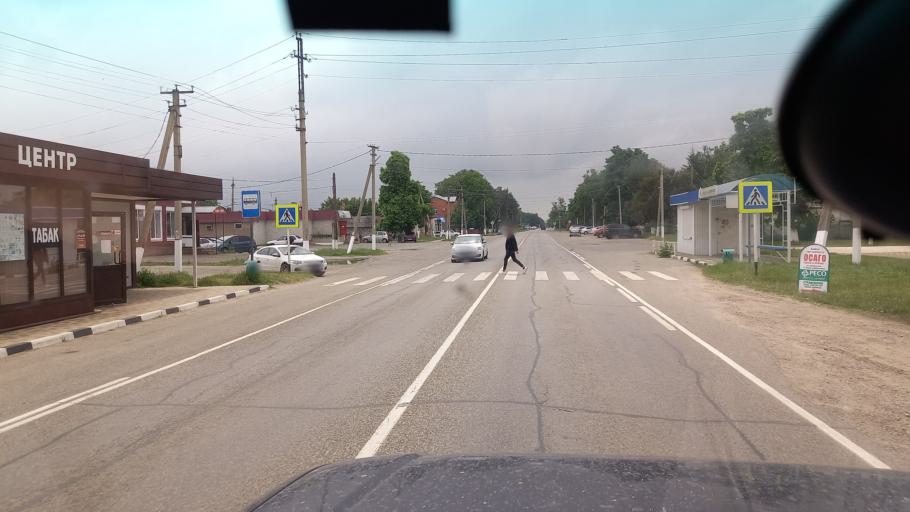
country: RU
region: Krasnodarskiy
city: Mostovskoy
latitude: 44.4126
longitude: 40.8030
